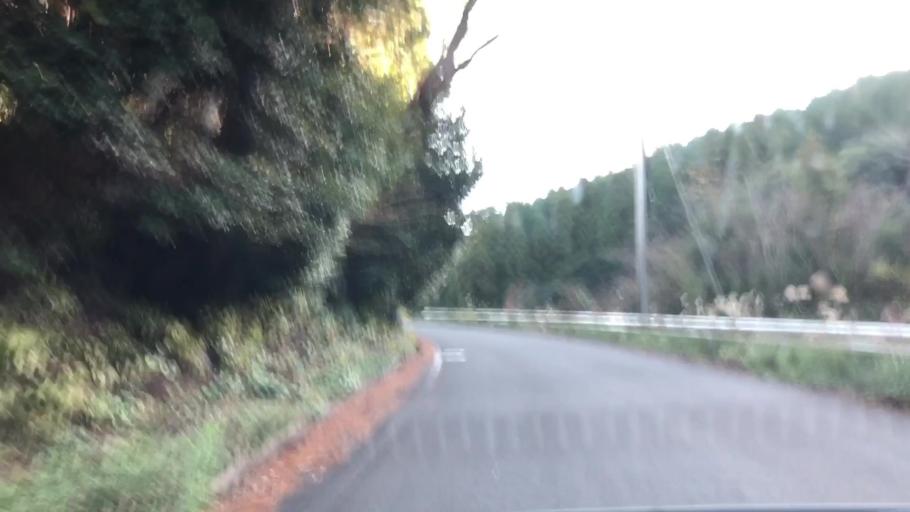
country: JP
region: Nagasaki
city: Sasebo
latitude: 33.0284
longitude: 129.6761
